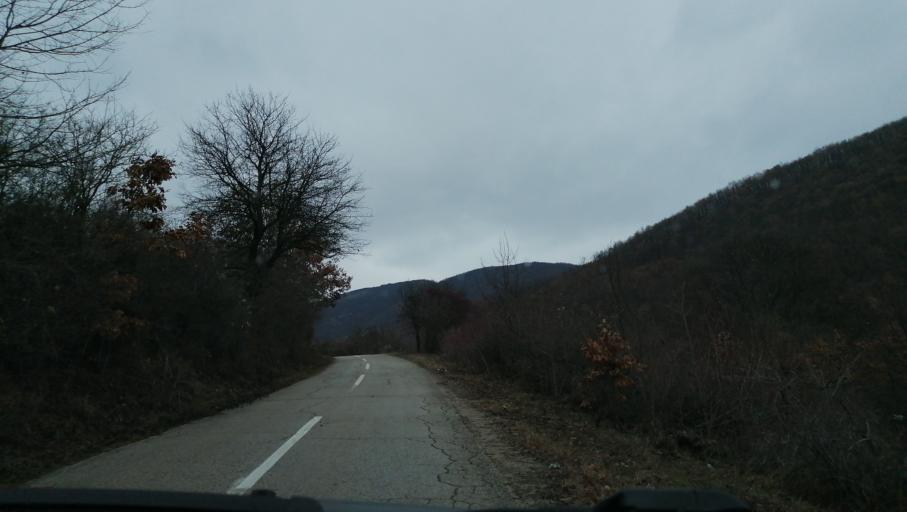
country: RS
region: Central Serbia
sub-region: Pirotski Okrug
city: Dimitrovgrad
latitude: 42.9674
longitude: 22.7841
